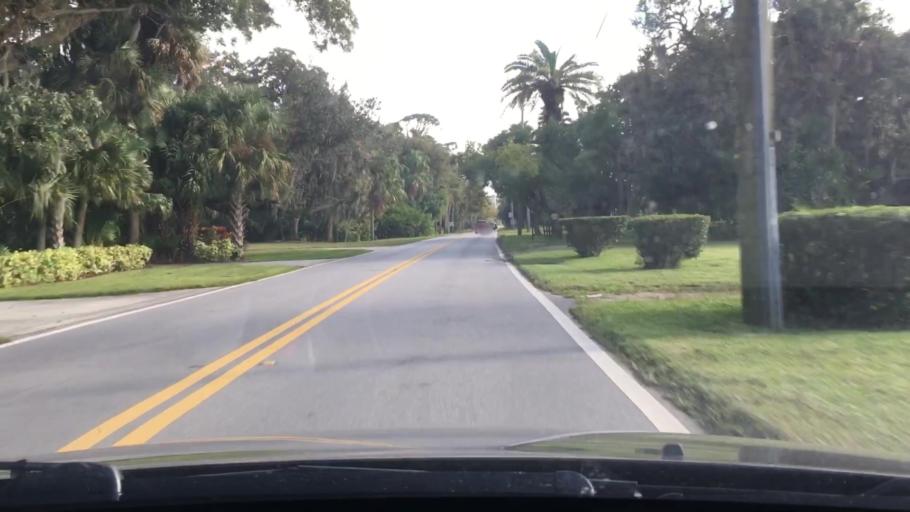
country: US
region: Florida
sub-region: Volusia County
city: Ormond Beach
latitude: 29.2967
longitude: -81.0513
